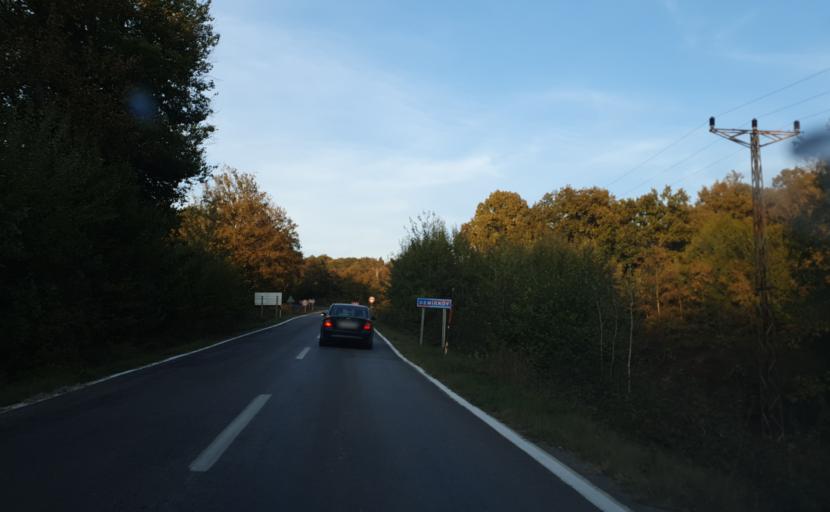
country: TR
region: Kirklareli
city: Sergen
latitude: 41.8353
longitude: 27.7936
